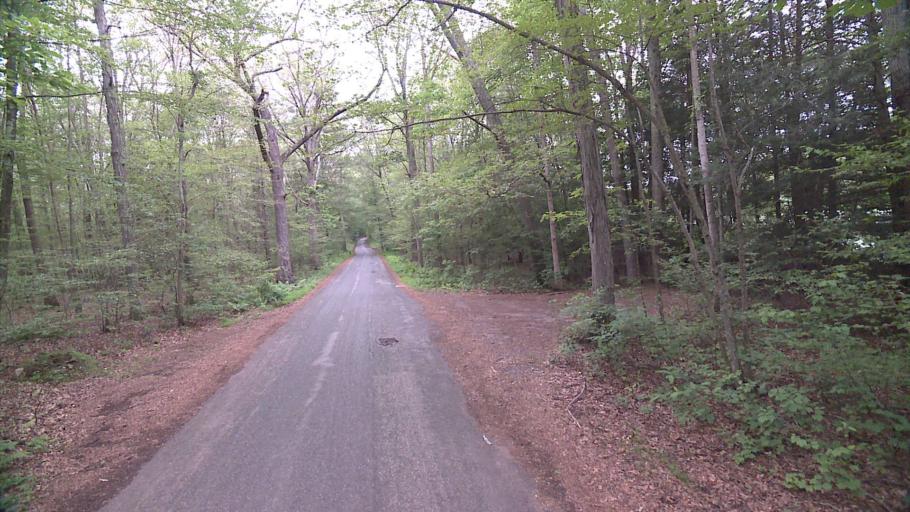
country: US
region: Connecticut
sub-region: Middlesex County
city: Moodus
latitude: 41.5554
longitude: -72.4181
